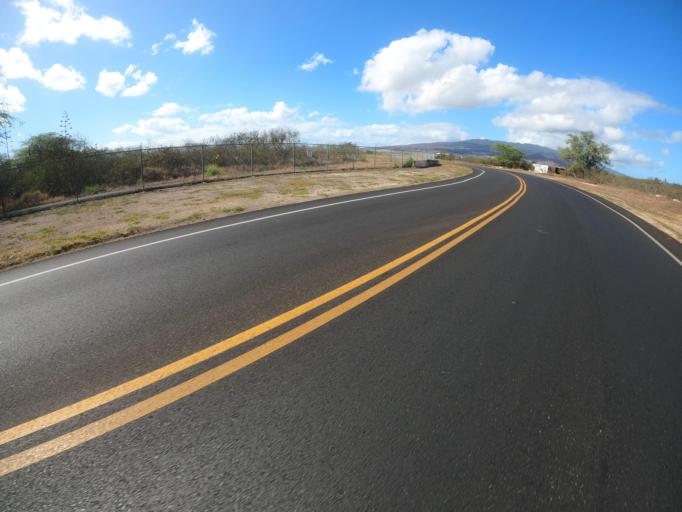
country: US
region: Hawaii
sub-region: Honolulu County
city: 'Ewa Villages
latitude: 21.3144
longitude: -158.0558
